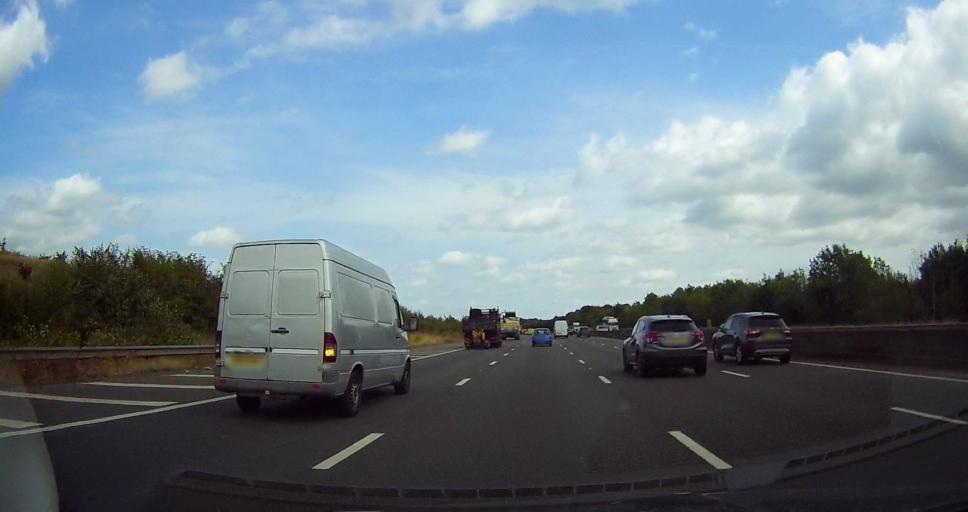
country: GB
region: England
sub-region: Kent
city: Westerham
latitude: 51.2731
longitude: 0.0492
